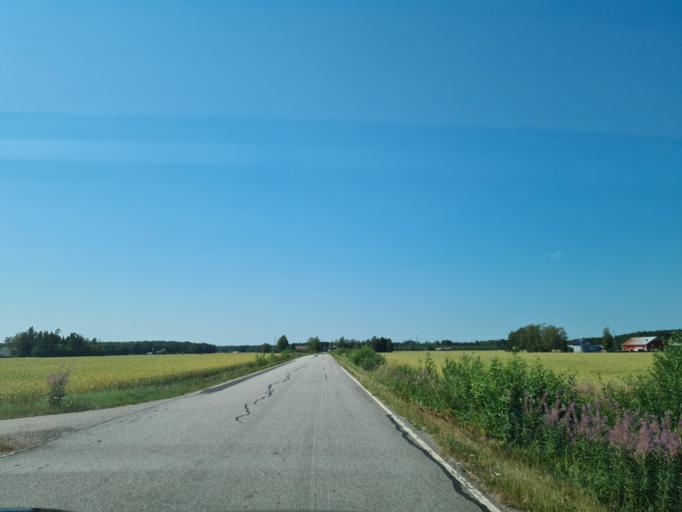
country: FI
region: Varsinais-Suomi
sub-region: Loimaa
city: Aura
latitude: 60.6029
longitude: 22.6459
